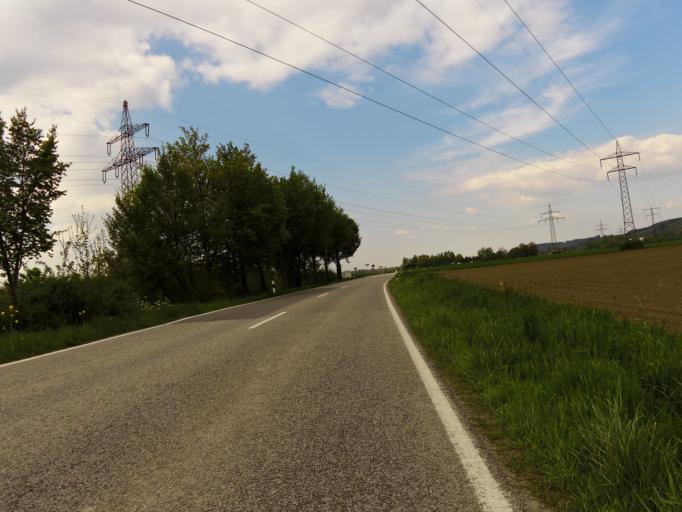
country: DE
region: Bavaria
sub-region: Upper Bavaria
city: Langenpreising
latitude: 48.4338
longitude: 11.9791
